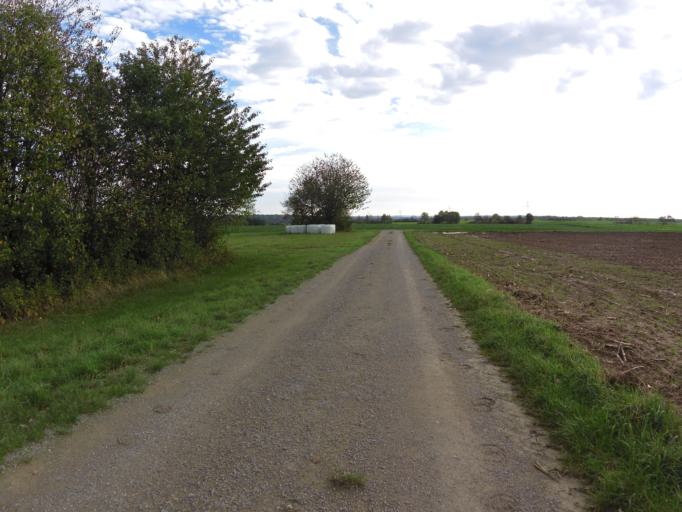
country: DE
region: Bavaria
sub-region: Regierungsbezirk Unterfranken
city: Biebelried
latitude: 49.7310
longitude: 10.0736
